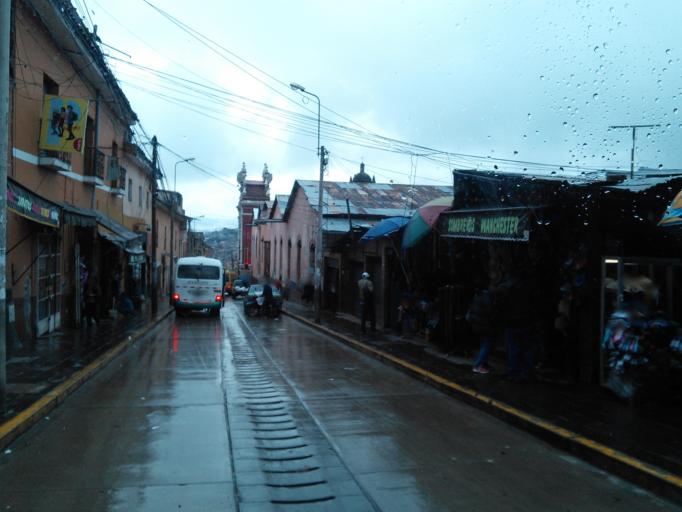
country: PE
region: Ayacucho
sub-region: Provincia de Huamanga
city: Ayacucho
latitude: -13.1629
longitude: -74.2280
